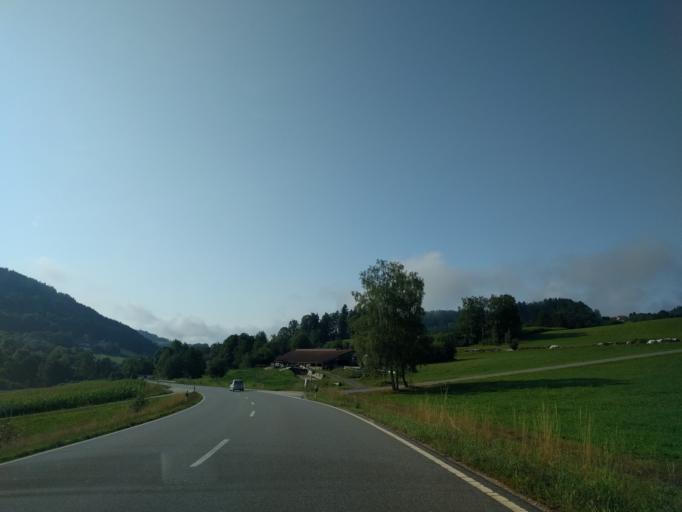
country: DE
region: Bavaria
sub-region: Lower Bavaria
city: Innernzell
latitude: 48.8542
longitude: 13.3039
